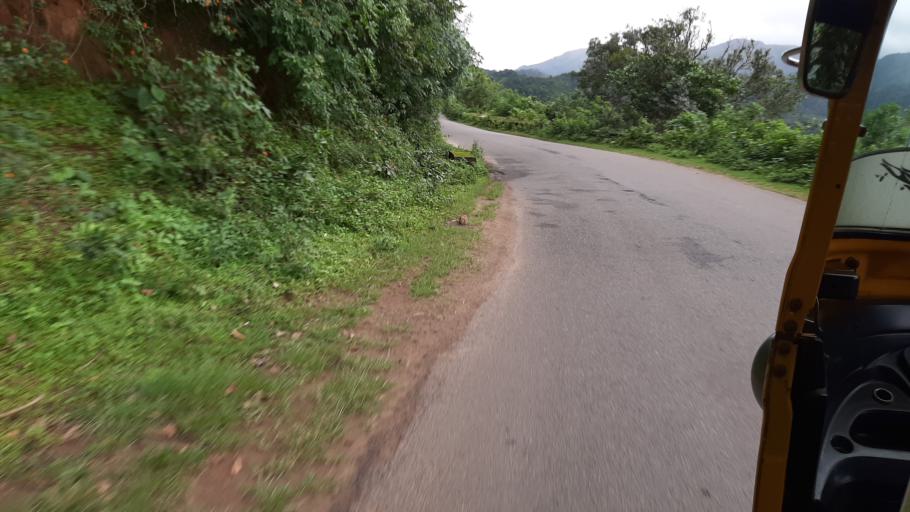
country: IN
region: Andhra Pradesh
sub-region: Vizianagaram District
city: Salur
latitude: 18.2462
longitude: 83.0219
